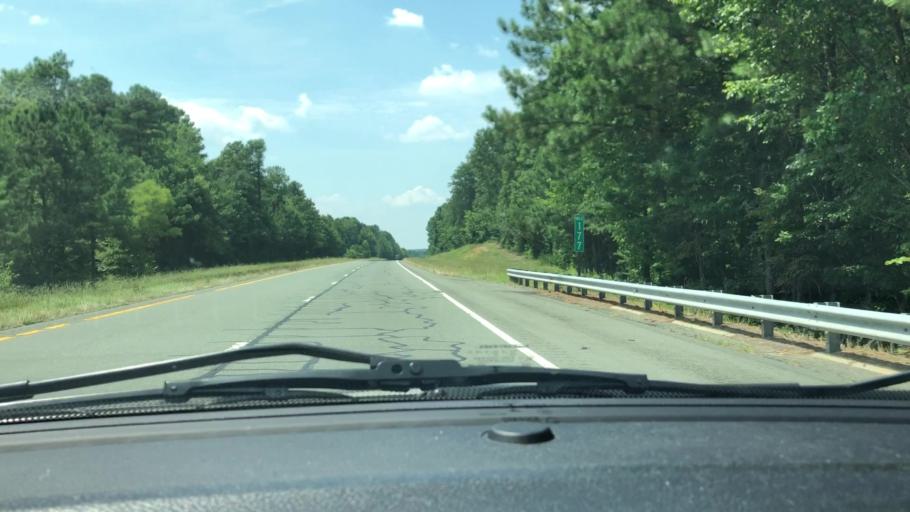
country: US
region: North Carolina
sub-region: Chatham County
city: Siler City
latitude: 35.7852
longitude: -79.5176
